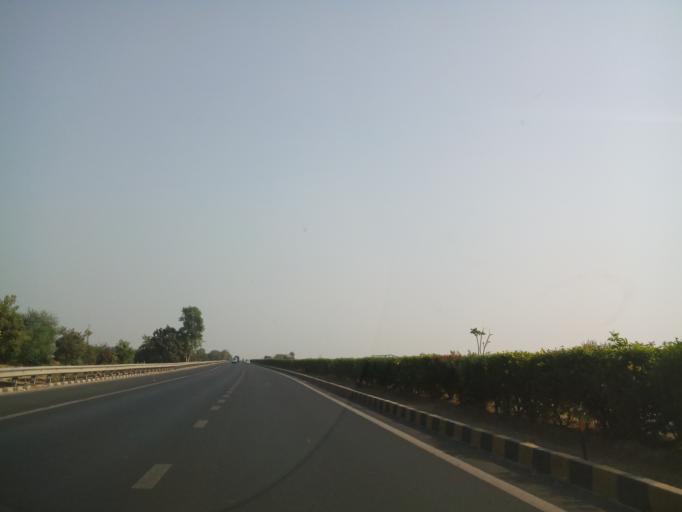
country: IN
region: Gujarat
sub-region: Ahmadabad
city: Ahmedabad
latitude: 22.9648
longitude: 72.6698
